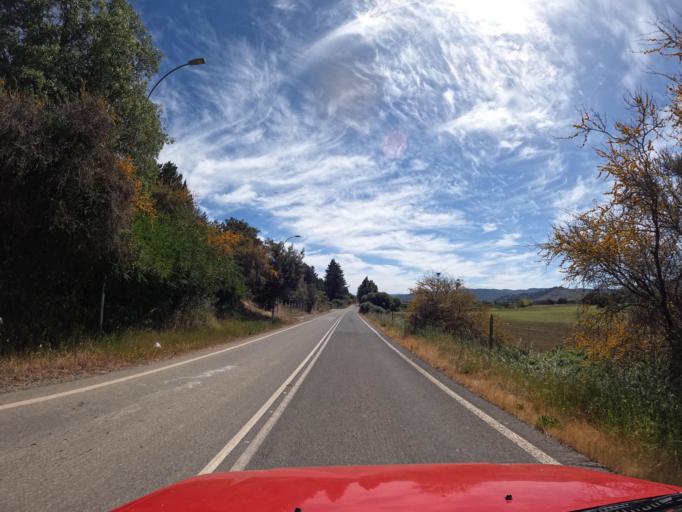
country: CL
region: Maule
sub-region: Provincia de Talca
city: Talca
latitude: -34.9893
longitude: -71.8129
